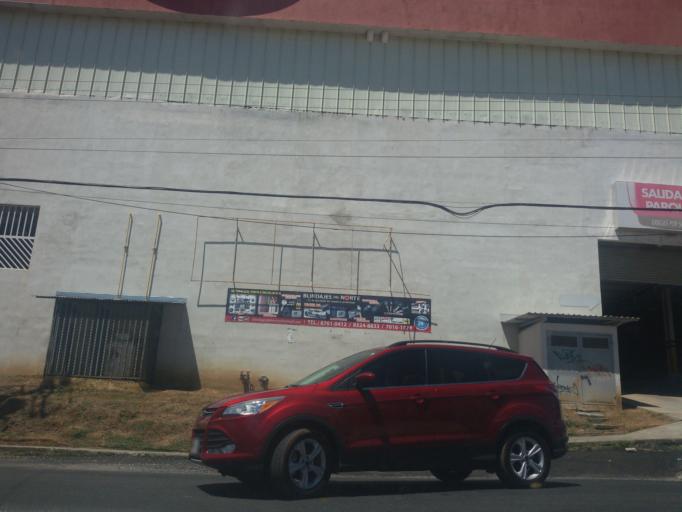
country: CR
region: Heredia
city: Heredia
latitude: 10.0015
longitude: -84.1116
